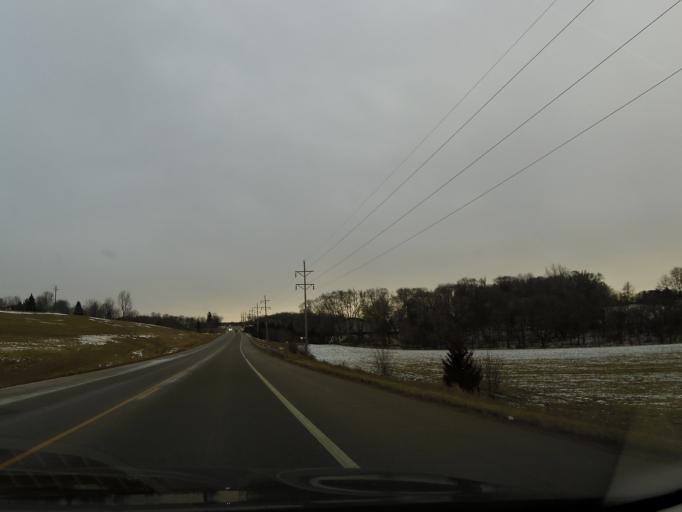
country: US
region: Minnesota
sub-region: Carver County
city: Waconia
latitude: 44.8856
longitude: -93.8171
